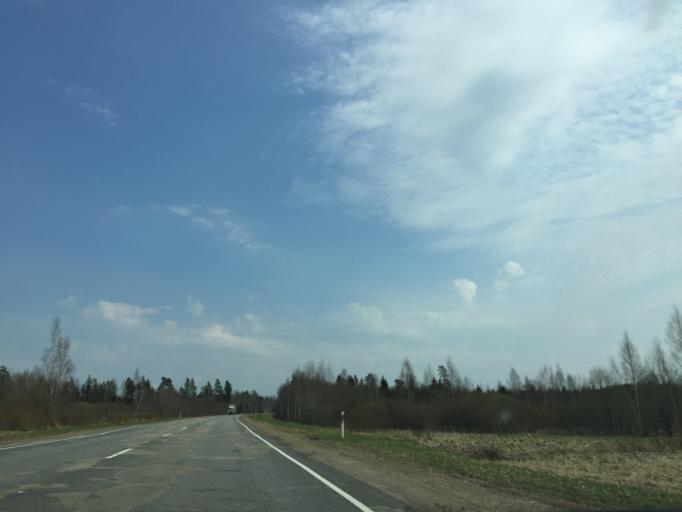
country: LV
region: Apes Novads
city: Ape
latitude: 57.4749
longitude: 26.4748
